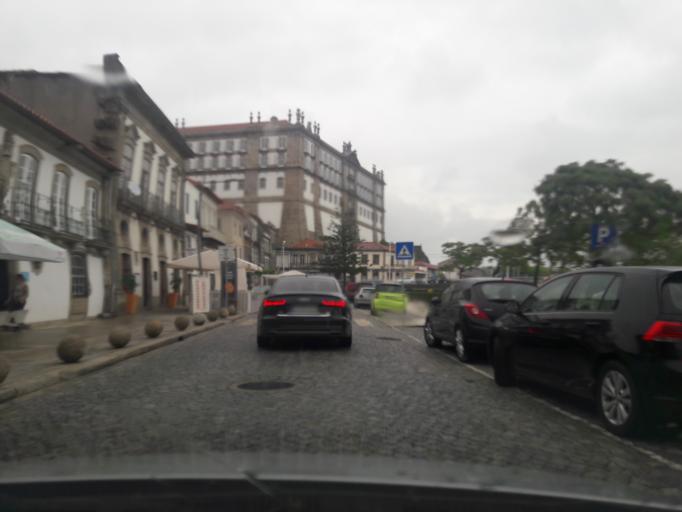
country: PT
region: Porto
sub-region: Vila do Conde
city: Vila do Conde
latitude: 41.3518
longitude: -8.7412
